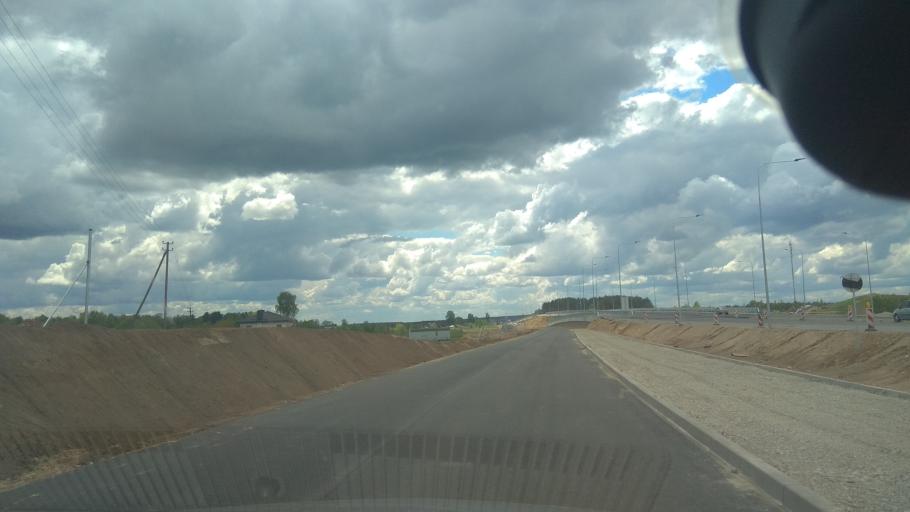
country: LT
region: Vilnius County
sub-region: Vilnius
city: Fabijoniskes
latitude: 54.8362
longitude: 25.2785
